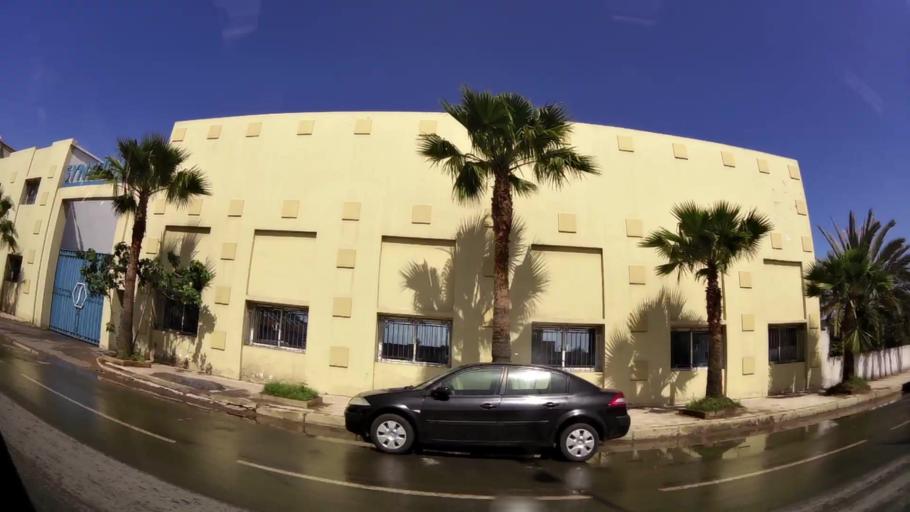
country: MA
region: Grand Casablanca
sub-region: Mediouna
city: Tit Mellil
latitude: 33.6189
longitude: -7.5149
